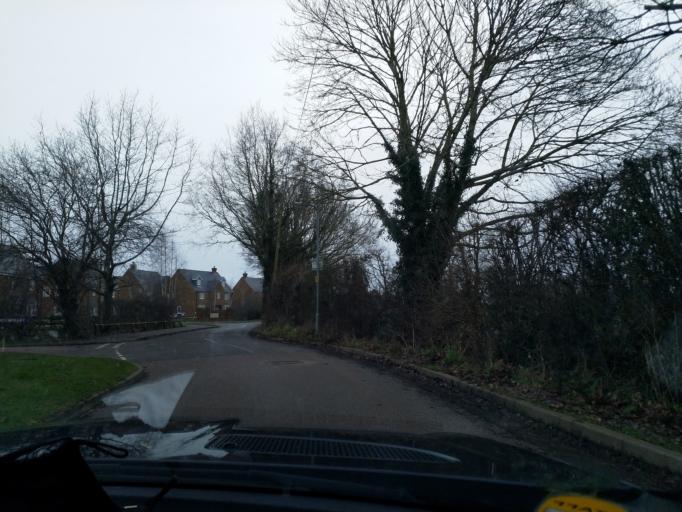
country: GB
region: England
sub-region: Oxfordshire
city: Adderbury
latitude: 52.0732
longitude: -1.2635
